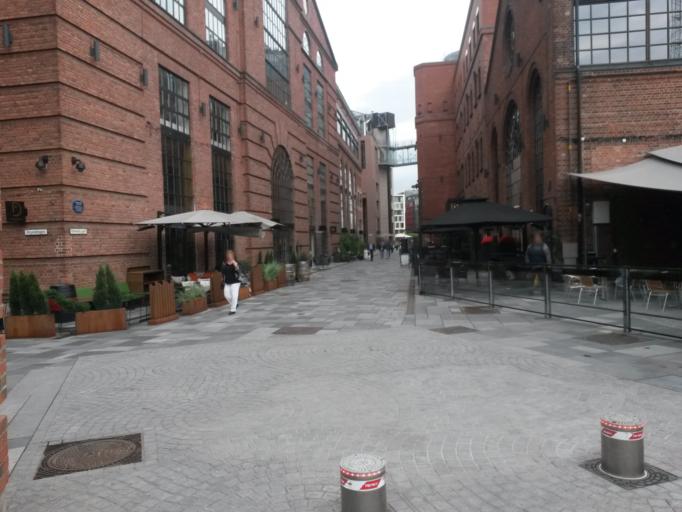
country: NO
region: Oslo
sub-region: Oslo
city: Oslo
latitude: 59.9110
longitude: 10.7272
